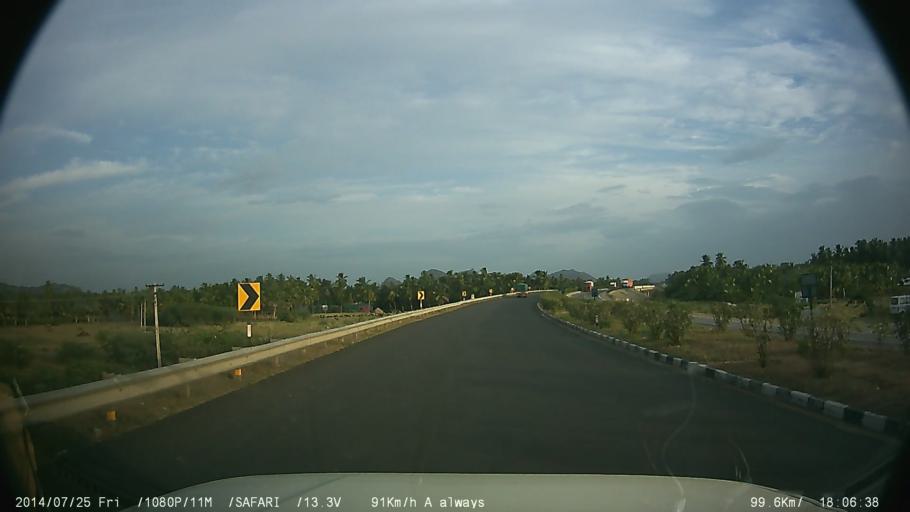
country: IN
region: Tamil Nadu
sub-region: Krishnagiri
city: Kaverippattanam
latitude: 12.4259
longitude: 78.2266
